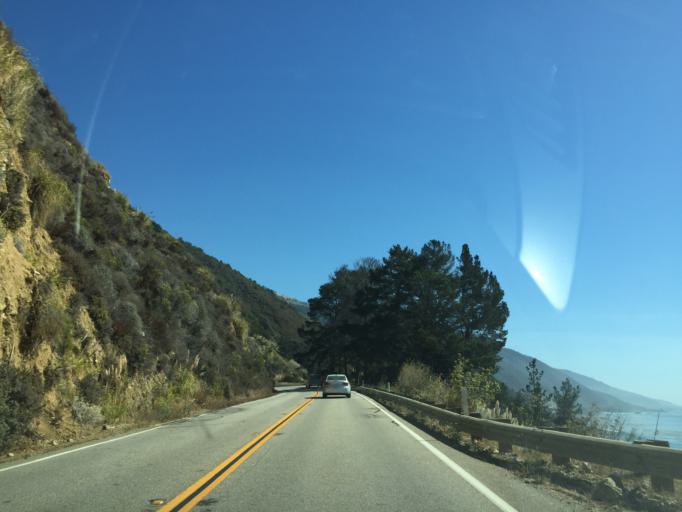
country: US
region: California
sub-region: Monterey County
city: Greenfield
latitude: 36.0015
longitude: -121.5035
